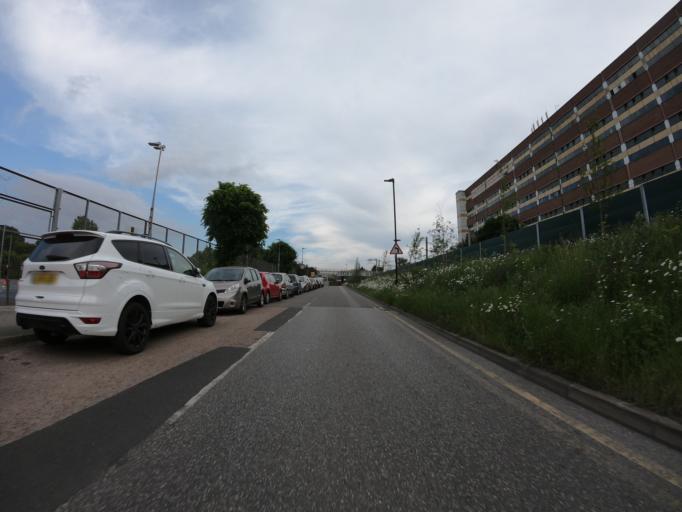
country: GB
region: England
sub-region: Greater London
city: Hackney
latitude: 51.5856
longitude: -0.0600
